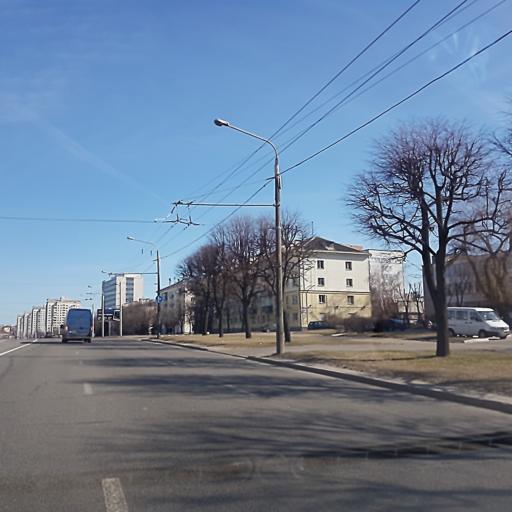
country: BY
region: Minsk
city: Minsk
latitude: 53.8803
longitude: 27.6025
